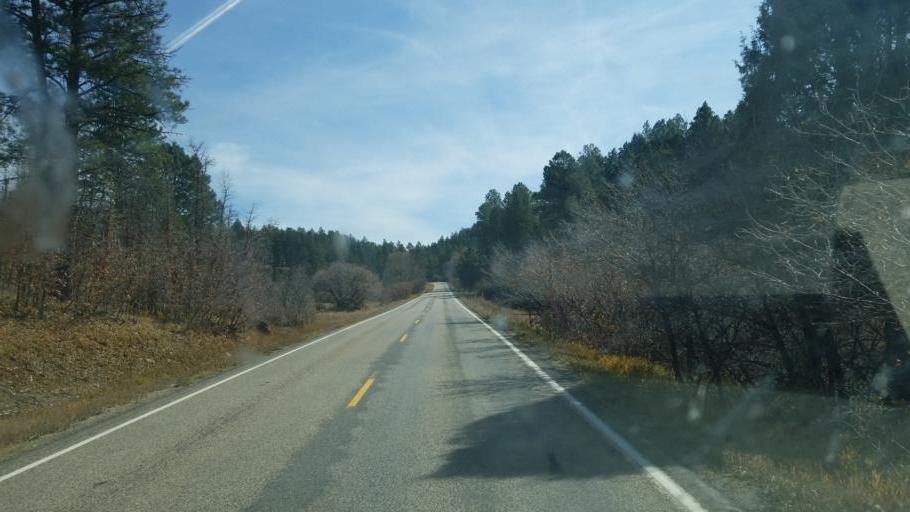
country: US
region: New Mexico
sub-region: Rio Arriba County
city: Dulce
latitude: 37.0767
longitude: -106.8513
